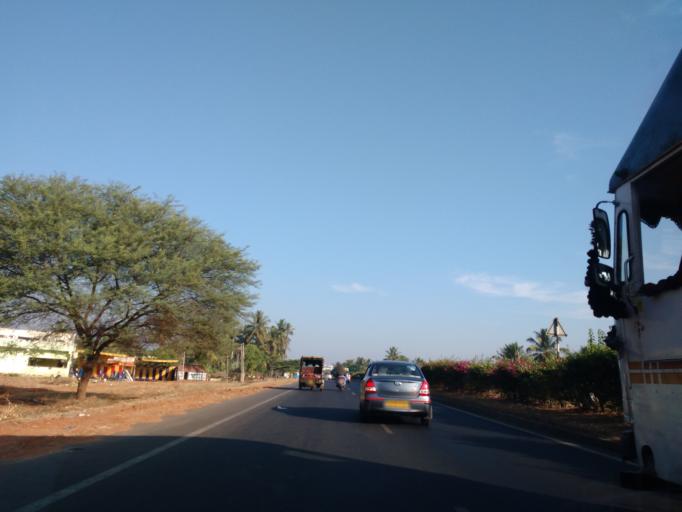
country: IN
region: Karnataka
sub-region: Bangalore Rural
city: Nelamangala
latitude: 13.1700
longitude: 77.3087
